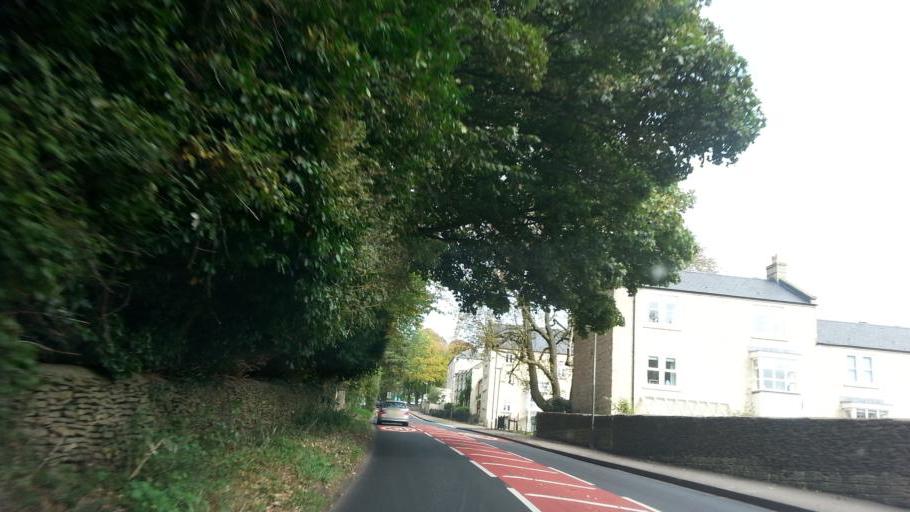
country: GB
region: England
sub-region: Gloucestershire
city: Painswick
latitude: 51.7830
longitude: -2.1984
